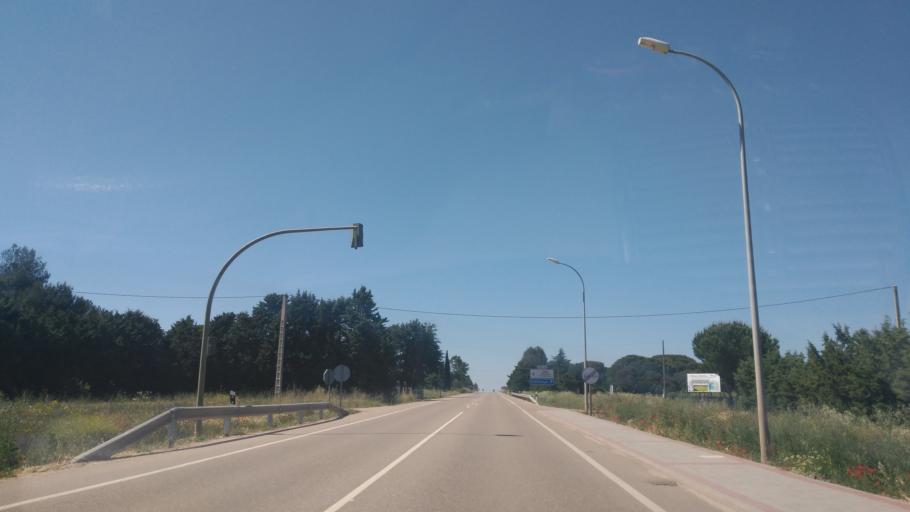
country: ES
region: Castille and Leon
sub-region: Provincia de Salamanca
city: Villares de la Reina
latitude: 41.0227
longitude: -5.6711
